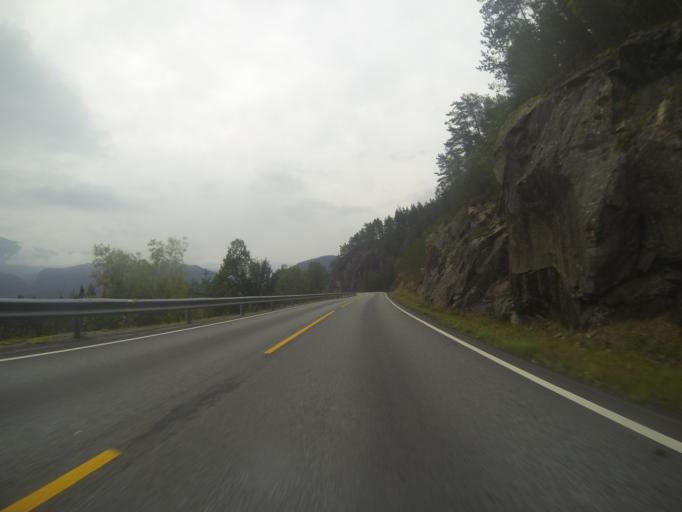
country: NO
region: Rogaland
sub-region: Suldal
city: Sand
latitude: 59.4697
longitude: 6.1800
